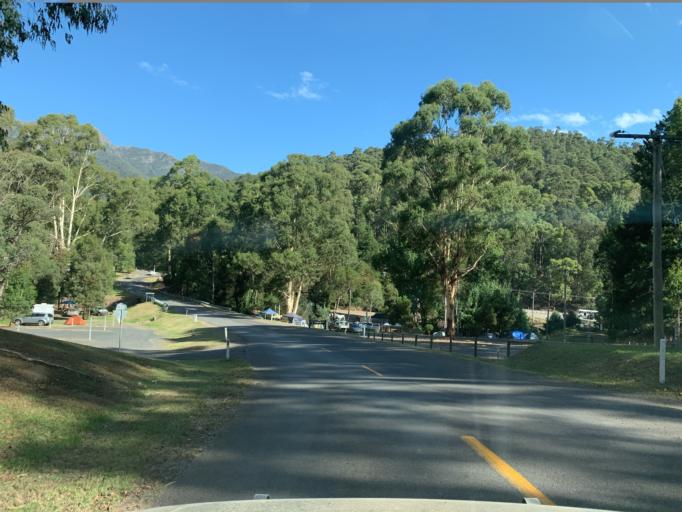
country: AU
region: Victoria
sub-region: Mansfield
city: Mansfield
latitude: -37.1083
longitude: 146.3992
